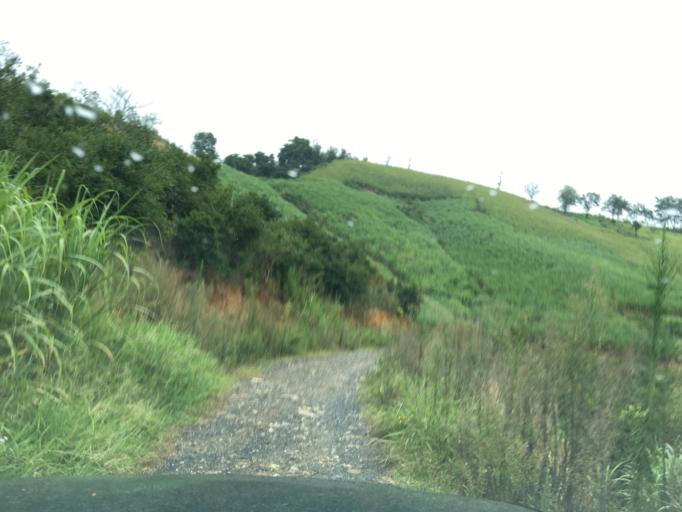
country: CN
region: Guangxi Zhuangzu Zizhiqu
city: Tongle
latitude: 25.0033
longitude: 105.9922
